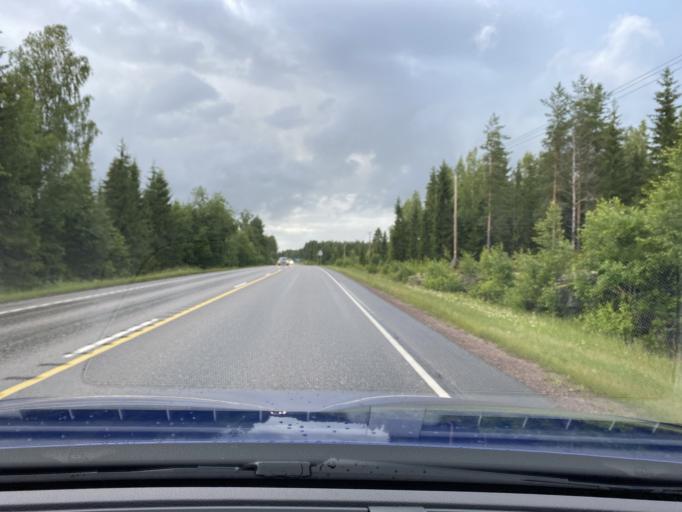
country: FI
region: Uusimaa
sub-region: Helsinki
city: Hyvinge
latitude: 60.5554
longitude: 24.8229
